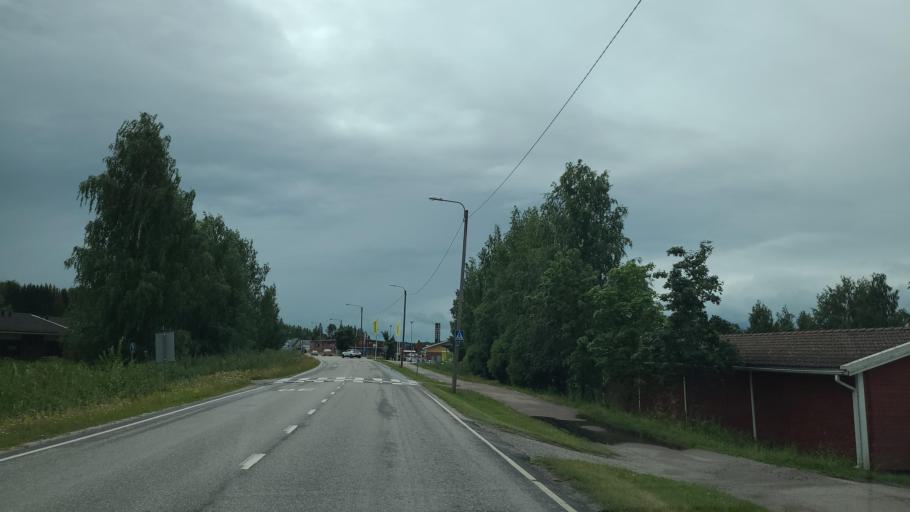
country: FI
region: Varsinais-Suomi
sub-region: Turku
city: Sauvo
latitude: 60.3434
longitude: 22.6907
